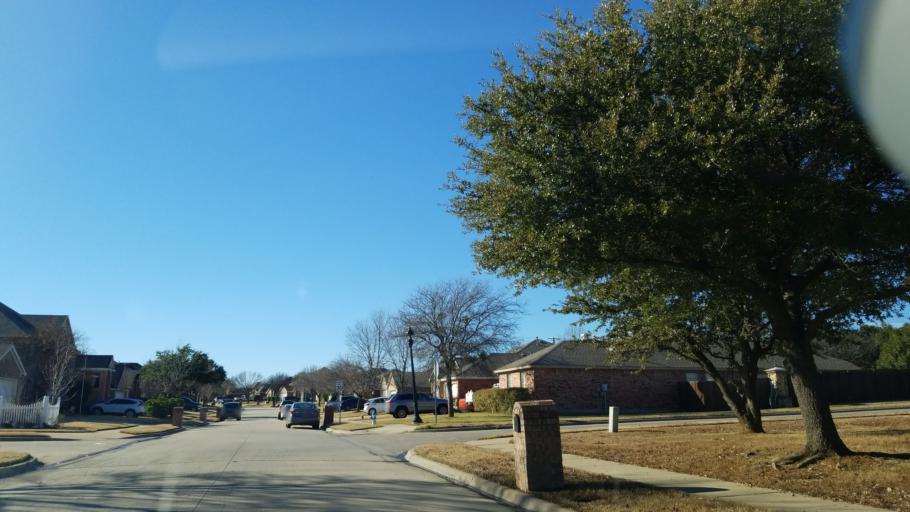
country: US
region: Texas
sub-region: Denton County
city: Corinth
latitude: 33.1417
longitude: -97.0830
